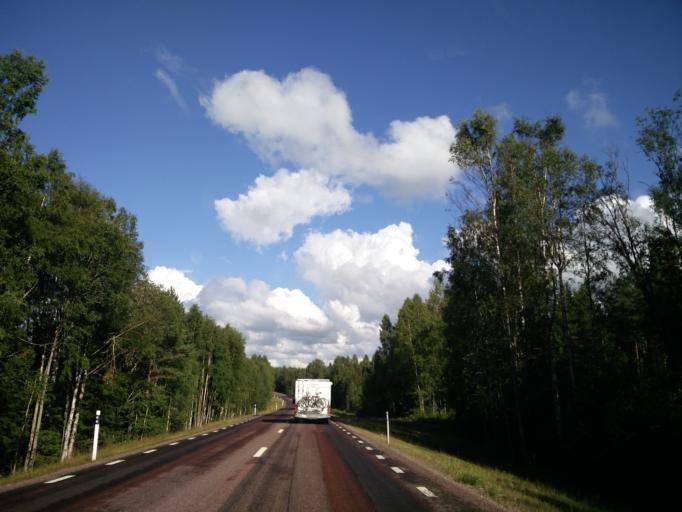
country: SE
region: Vaermland
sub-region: Hagfors Kommun
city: Ekshaerad
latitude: 60.4798
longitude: 13.3240
